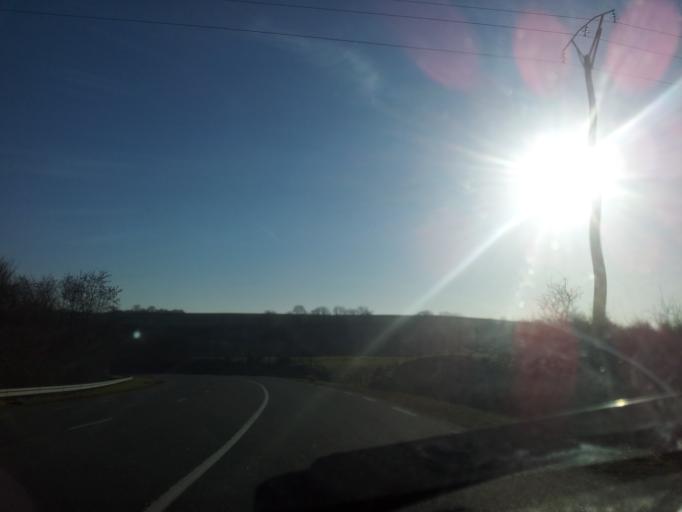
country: FR
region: Auvergne
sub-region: Departement de l'Allier
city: Saint-Pourcain-sur-Sioule
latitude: 46.3132
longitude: 3.2199
